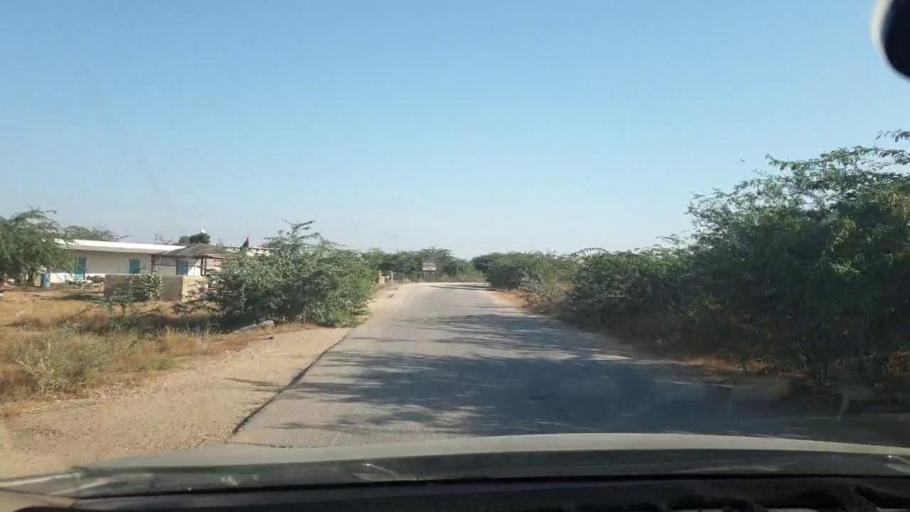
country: PK
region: Sindh
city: Malir Cantonment
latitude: 25.1752
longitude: 67.2033
